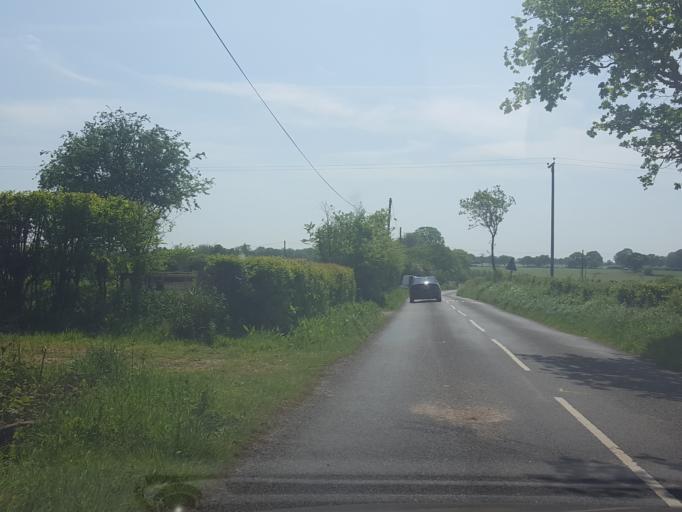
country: GB
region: England
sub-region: Essex
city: Great Bentley
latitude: 51.8559
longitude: 1.0858
